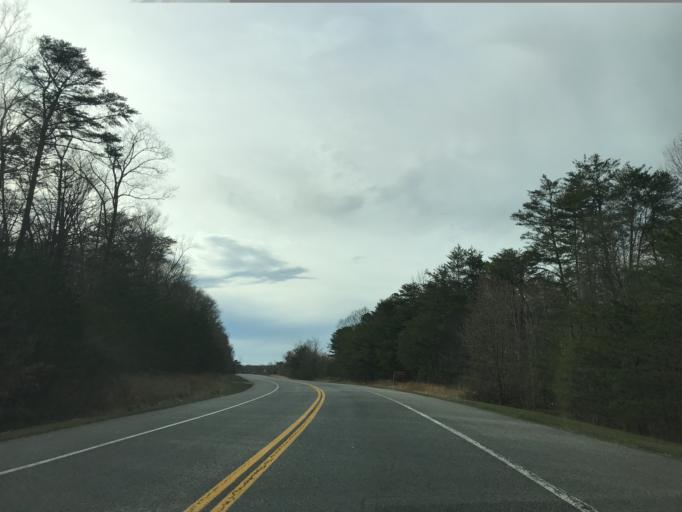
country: US
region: Maryland
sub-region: Prince George's County
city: Glenn Dale
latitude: 39.0294
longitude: -76.7784
